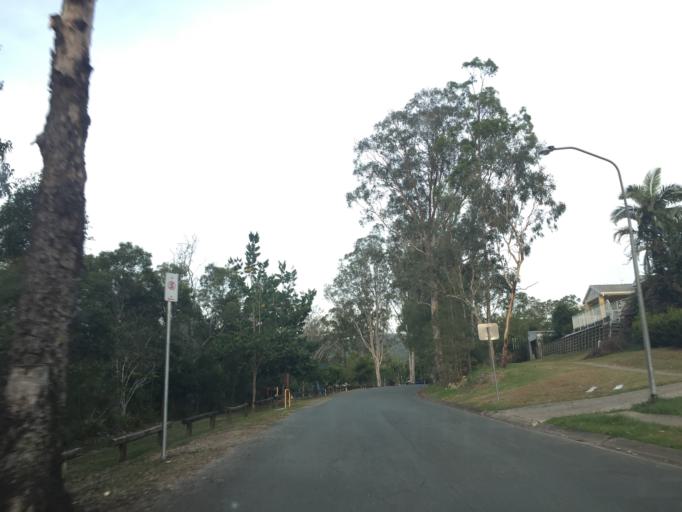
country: AU
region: Queensland
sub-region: Moreton Bay
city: Ferny Hills
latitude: -27.4397
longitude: 152.9336
